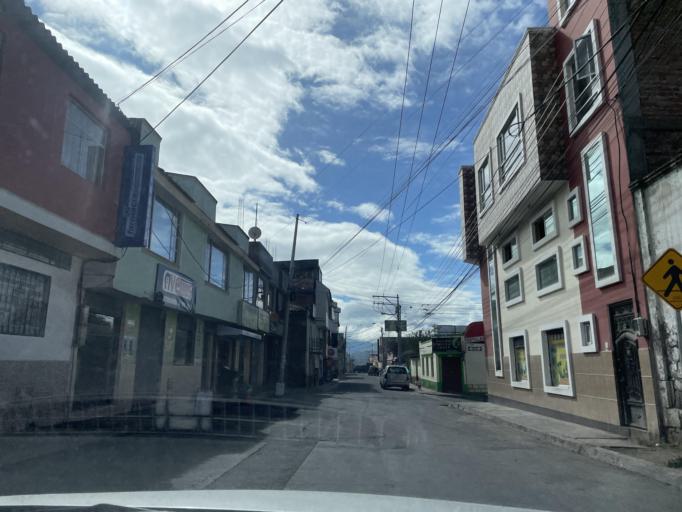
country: EC
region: Chimborazo
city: Guano
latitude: -1.6065
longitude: -78.6463
